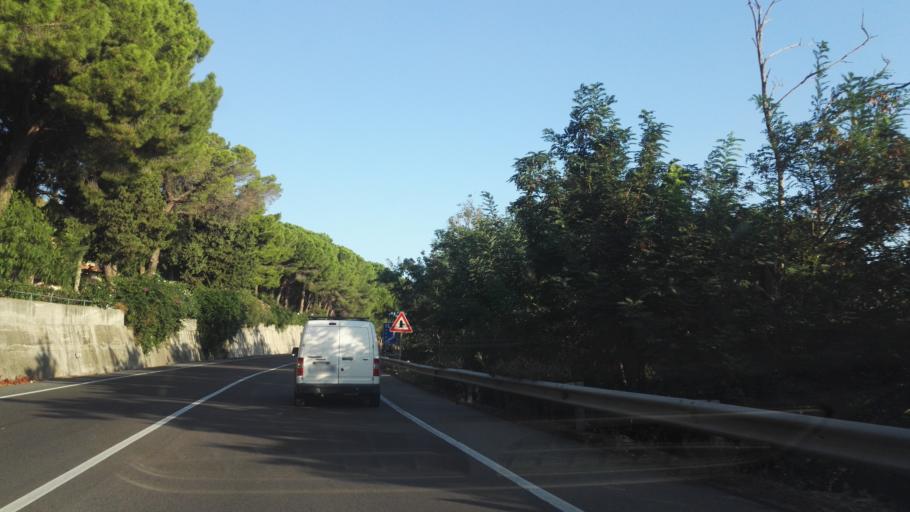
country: IT
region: Calabria
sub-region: Provincia di Catanzaro
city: Squillace Lido
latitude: 38.7673
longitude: 16.5622
